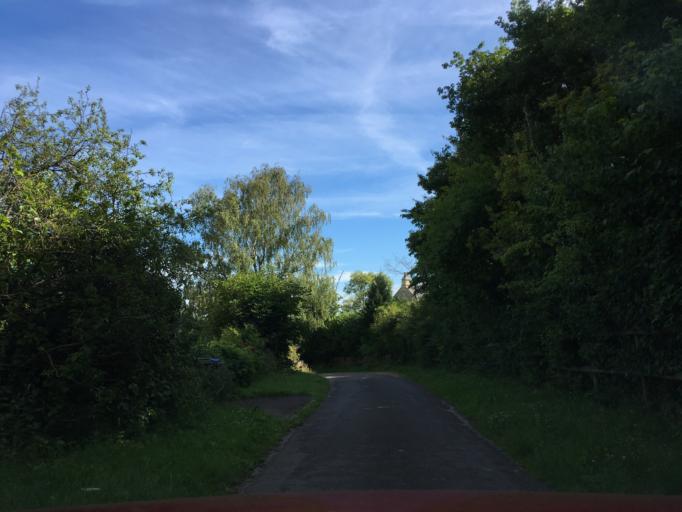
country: GB
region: England
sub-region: Wiltshire
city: Nettleton
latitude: 51.4868
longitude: -2.2656
